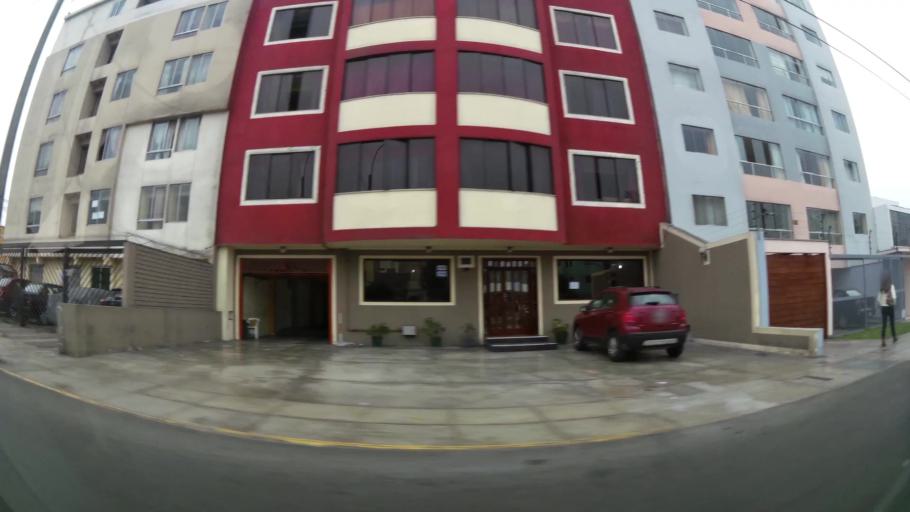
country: PE
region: Lima
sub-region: Lima
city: San Isidro
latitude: -12.0726
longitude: -77.0676
